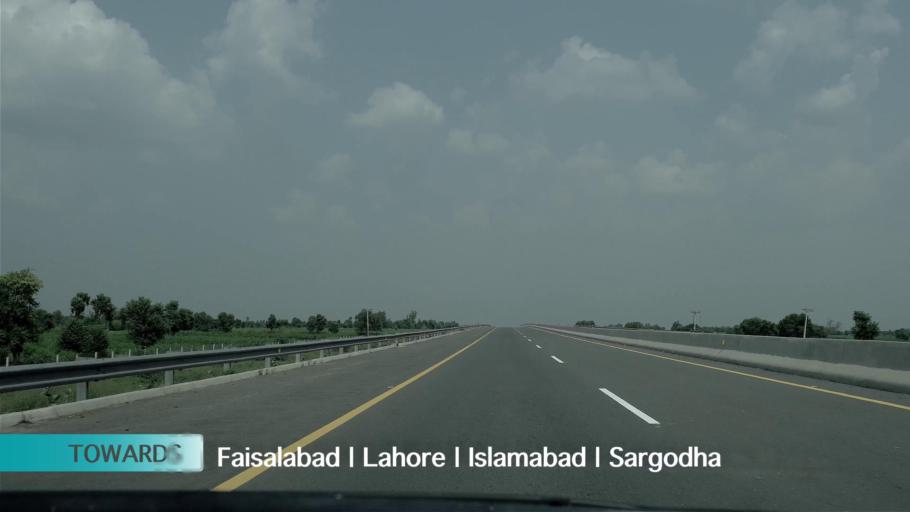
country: PK
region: Punjab
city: Gojra
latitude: 31.1971
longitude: 72.6556
